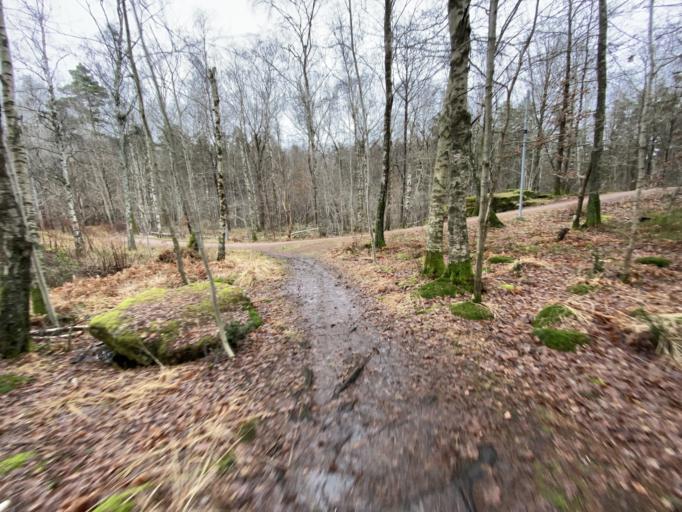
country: SE
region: Vaestra Goetaland
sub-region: Goteborg
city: Eriksbo
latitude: 57.7116
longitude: 12.0476
